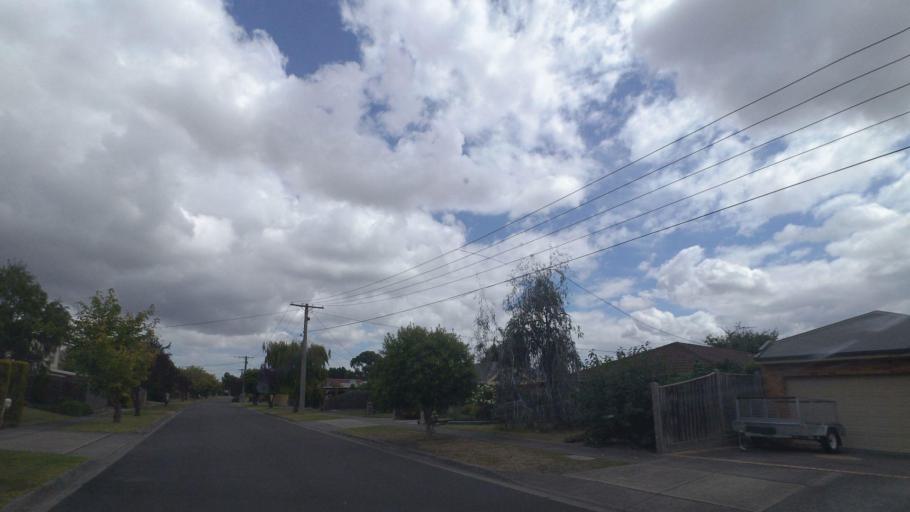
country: AU
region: Victoria
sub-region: Knox
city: Scoresby
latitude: -37.9160
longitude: 145.2315
